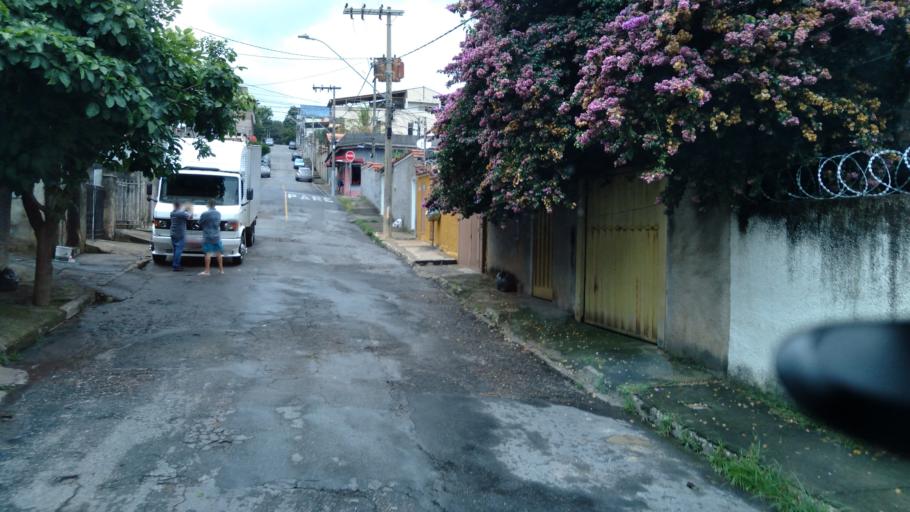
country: BR
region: Minas Gerais
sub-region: Belo Horizonte
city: Belo Horizonte
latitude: -19.9147
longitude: -43.8980
